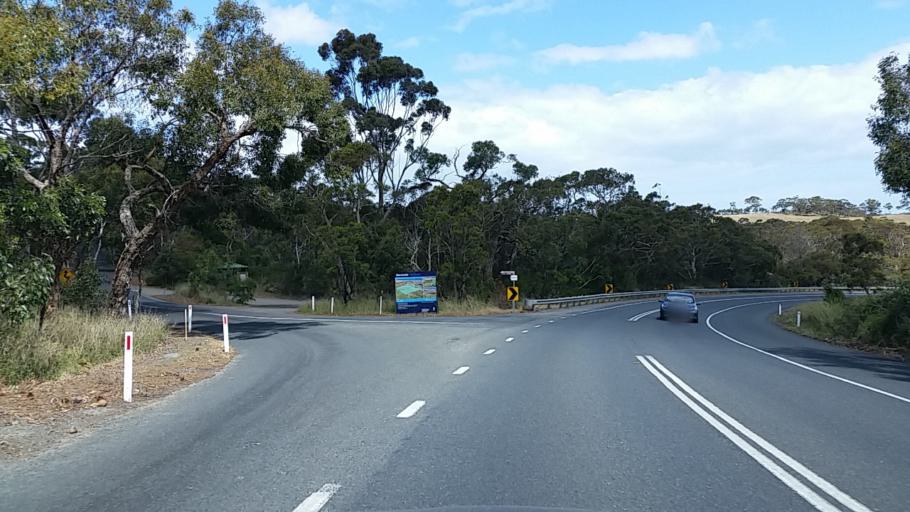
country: AU
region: South Australia
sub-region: Alexandrina
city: Port Elliot
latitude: -35.4617
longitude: 138.6488
